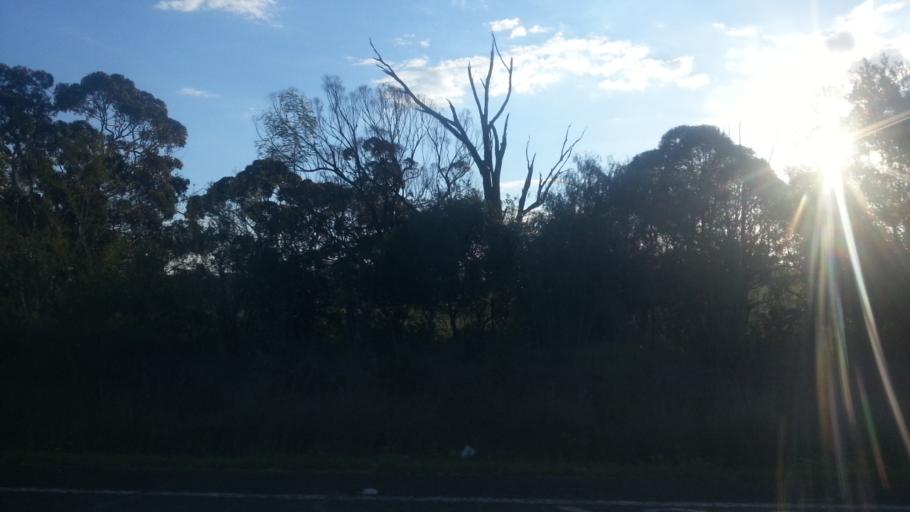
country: AU
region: New South Wales
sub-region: Wollondilly
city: Douglas Park
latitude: -34.1449
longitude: 150.7186
